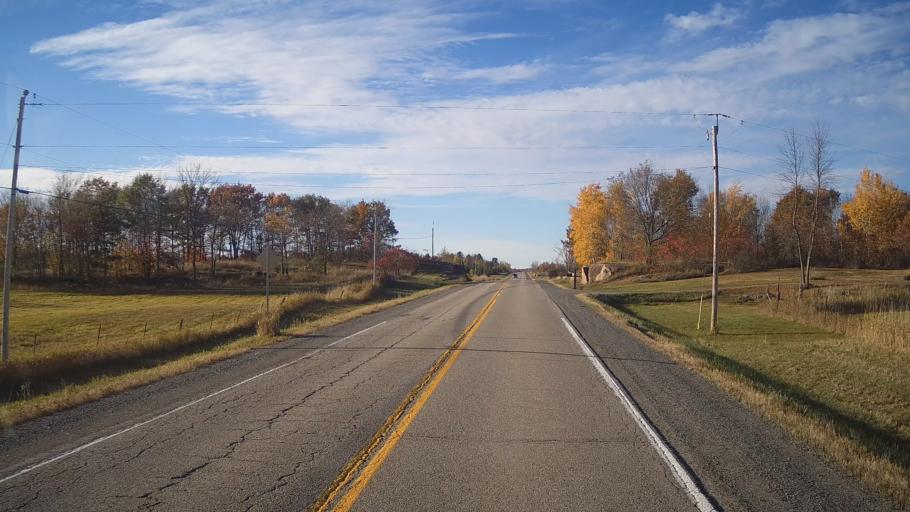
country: CA
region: Ontario
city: Perth
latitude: 44.7081
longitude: -76.4323
